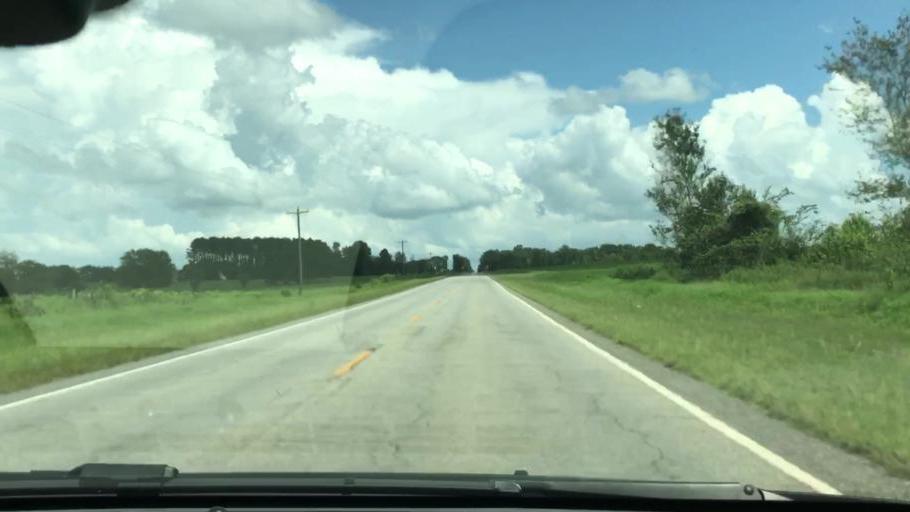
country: US
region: Georgia
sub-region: Seminole County
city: Donalsonville
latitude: 30.9804
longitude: -84.9869
